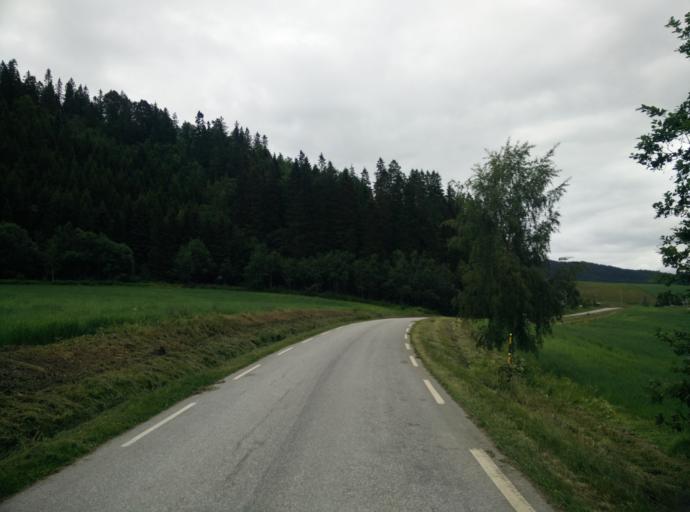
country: NO
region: Sor-Trondelag
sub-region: Skaun
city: Borsa
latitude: 63.3213
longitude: 10.0769
